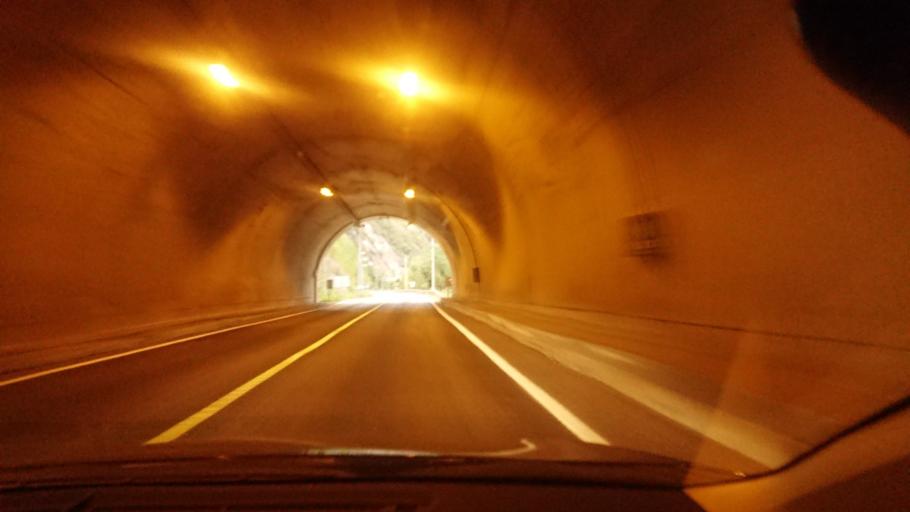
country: TR
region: Karabuk
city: Yenice
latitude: 41.1701
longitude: 32.4491
